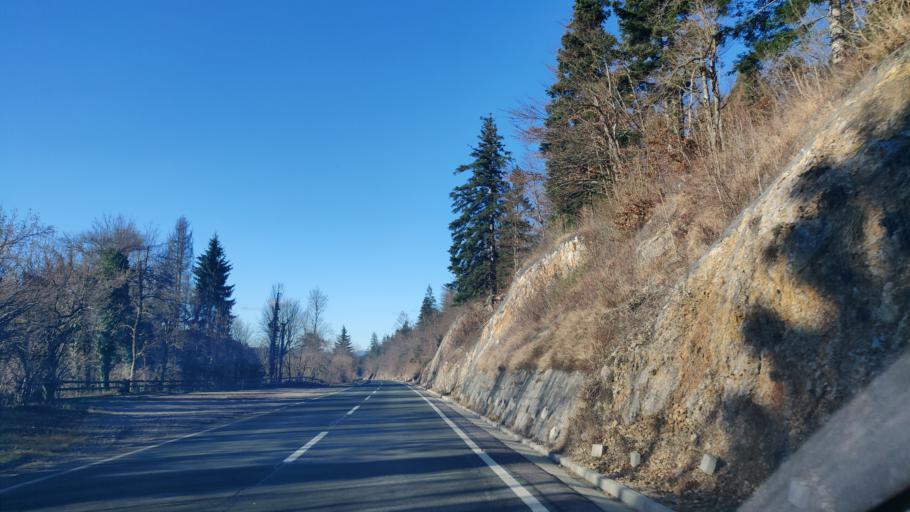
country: SI
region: Logatec
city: Logatec
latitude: 45.8864
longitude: 14.2006
